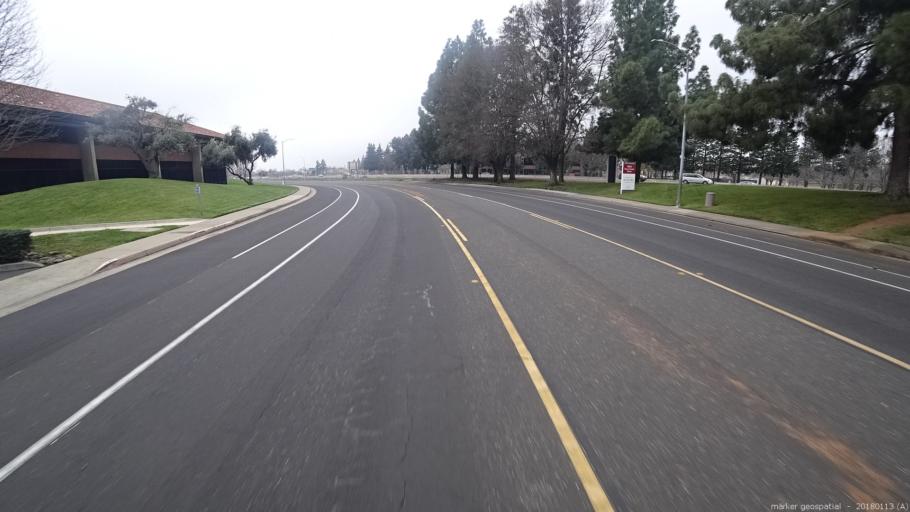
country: US
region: California
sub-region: Sacramento County
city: Rancho Cordova
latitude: 38.5949
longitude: -121.2798
